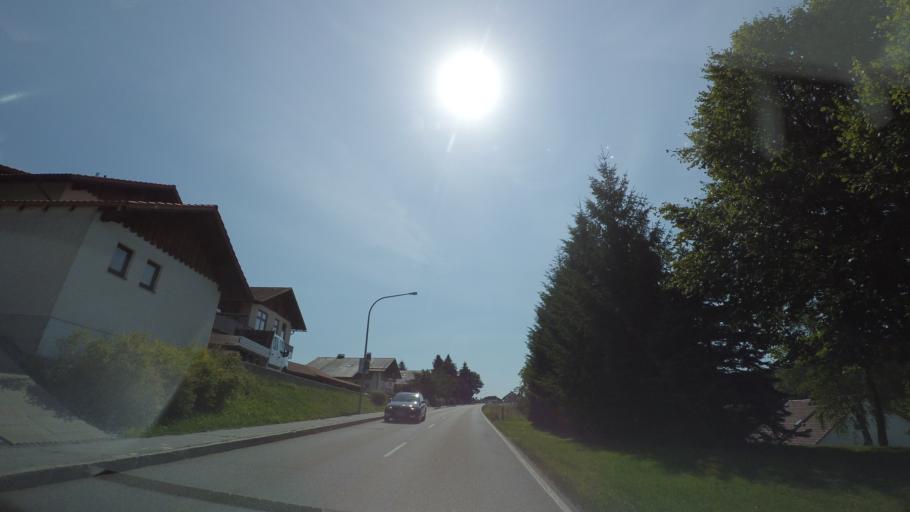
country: DE
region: Bavaria
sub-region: Lower Bavaria
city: Geiersthal
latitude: 49.0469
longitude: 12.9778
